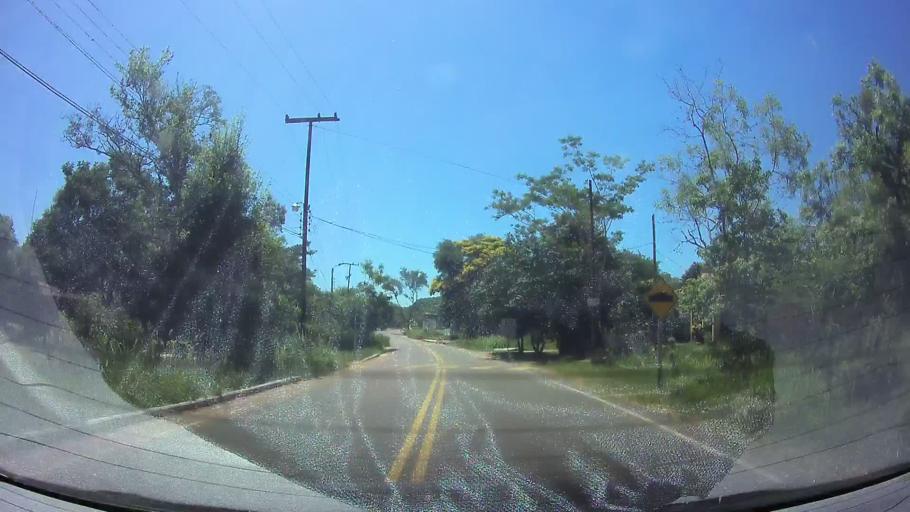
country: PY
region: Central
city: Aregua
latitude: -25.2602
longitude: -57.4434
